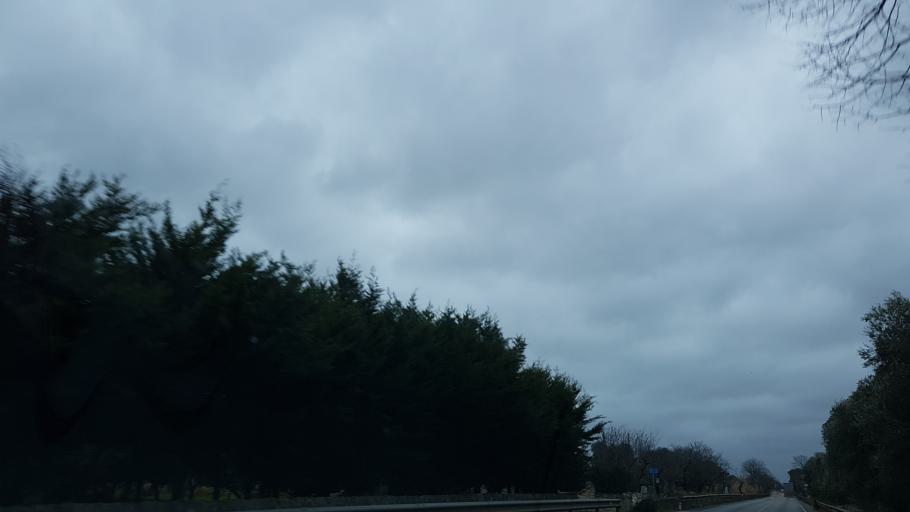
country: IT
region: Apulia
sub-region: Provincia di Brindisi
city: San Vito dei Normanni
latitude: 40.6566
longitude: 17.7360
